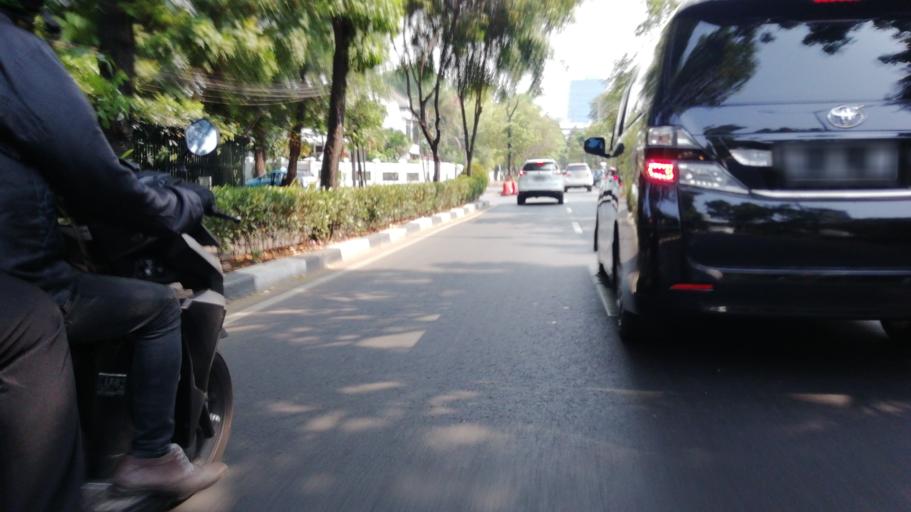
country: ID
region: Jakarta Raya
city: Jakarta
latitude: -6.2307
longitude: 106.8007
